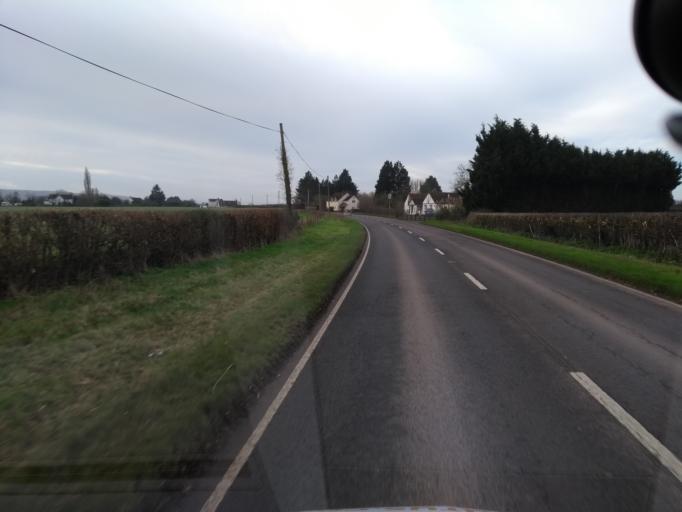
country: GB
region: England
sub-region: Somerset
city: Westonzoyland
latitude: 51.1183
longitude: -2.8513
